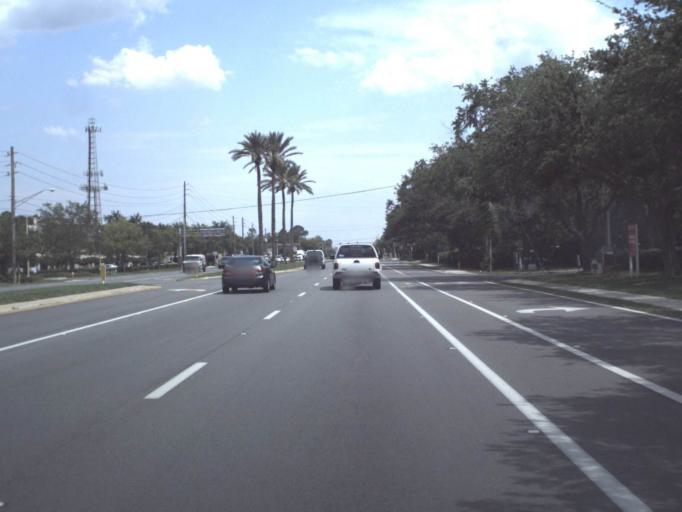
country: US
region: Florida
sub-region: Duval County
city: Jacksonville
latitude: 30.2849
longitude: -81.6318
